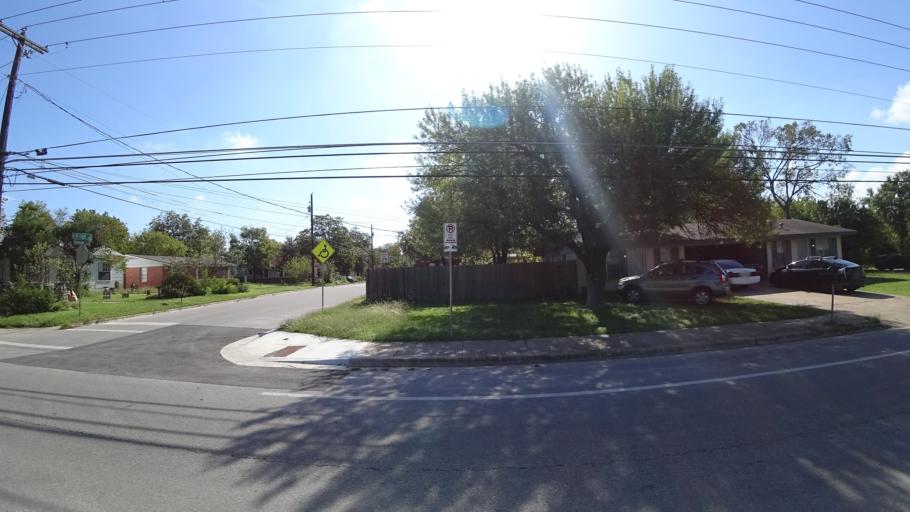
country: US
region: Texas
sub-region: Travis County
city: Austin
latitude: 30.3385
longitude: -97.7140
